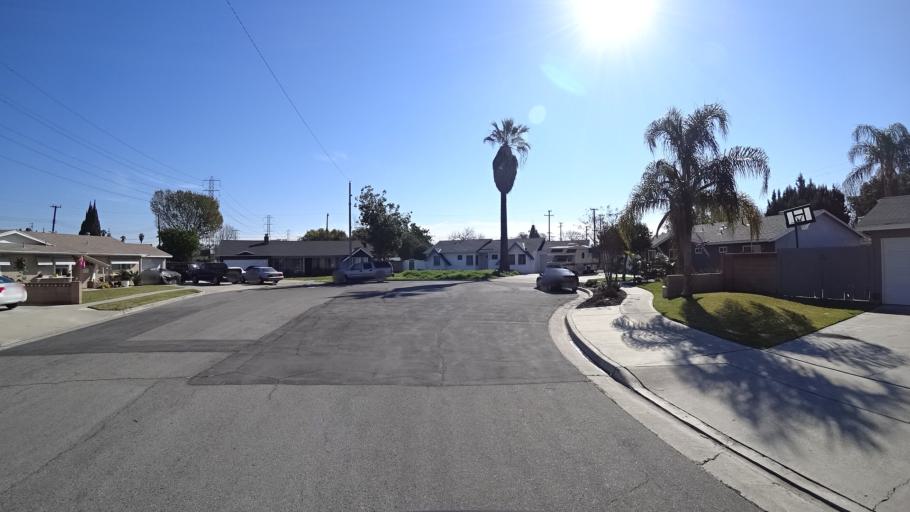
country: US
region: California
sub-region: Orange County
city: Garden Grove
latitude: 33.8065
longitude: -117.9357
